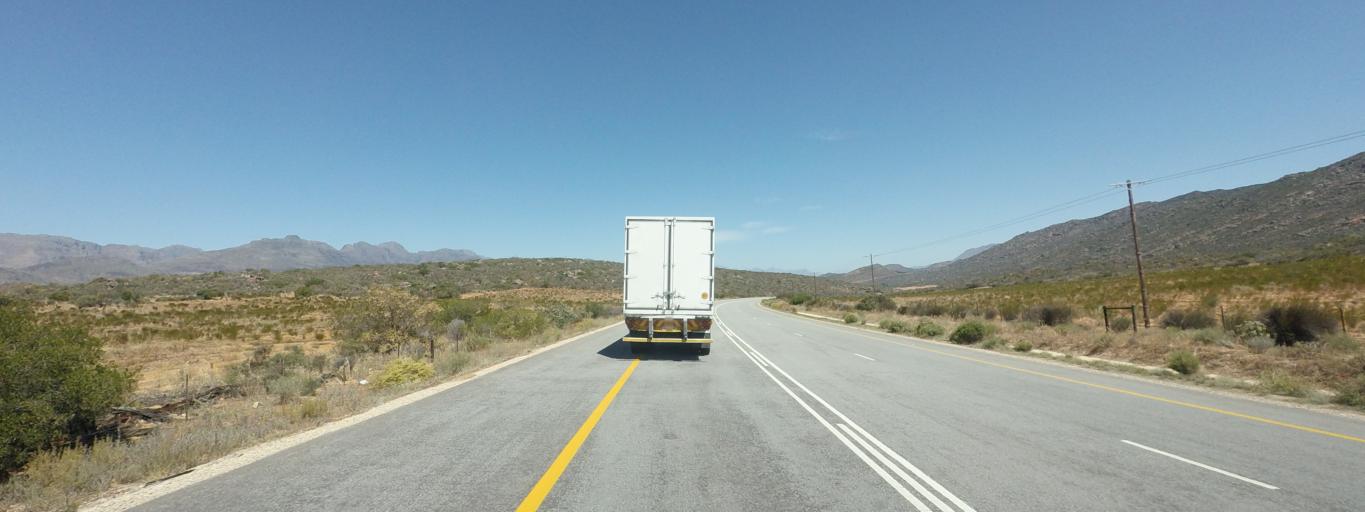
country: ZA
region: Western Cape
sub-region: West Coast District Municipality
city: Clanwilliam
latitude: -32.3280
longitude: 18.9228
